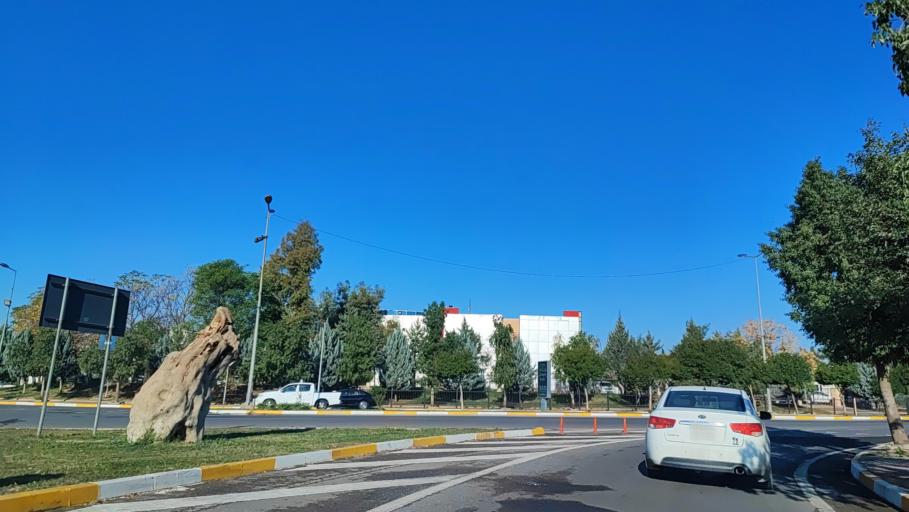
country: IQ
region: Arbil
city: Erbil
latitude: 36.1798
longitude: 44.0034
